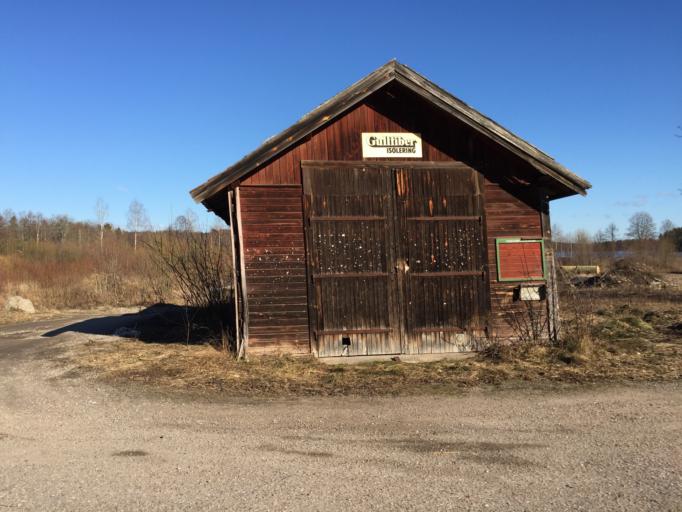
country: SE
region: Soedermanland
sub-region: Vingakers Kommun
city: Vingaker
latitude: 58.9941
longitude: 15.8202
